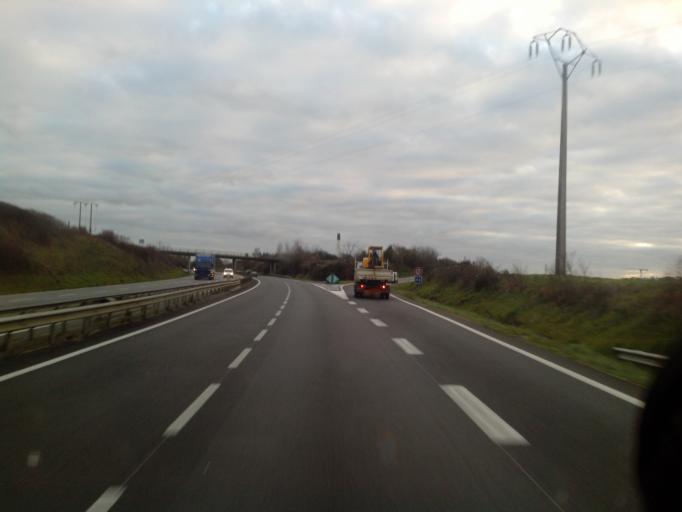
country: FR
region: Poitou-Charentes
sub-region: Departement de la Vienne
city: Montamise
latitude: 46.5997
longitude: 0.3912
